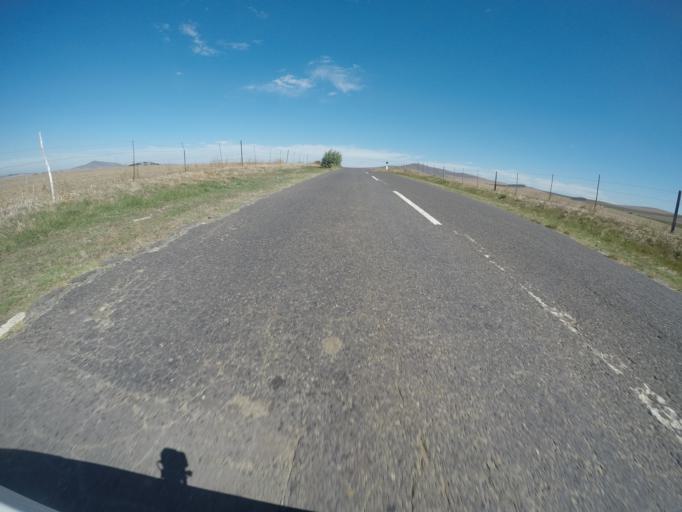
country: ZA
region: Western Cape
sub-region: City of Cape Town
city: Atlantis
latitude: -33.6843
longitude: 18.6004
